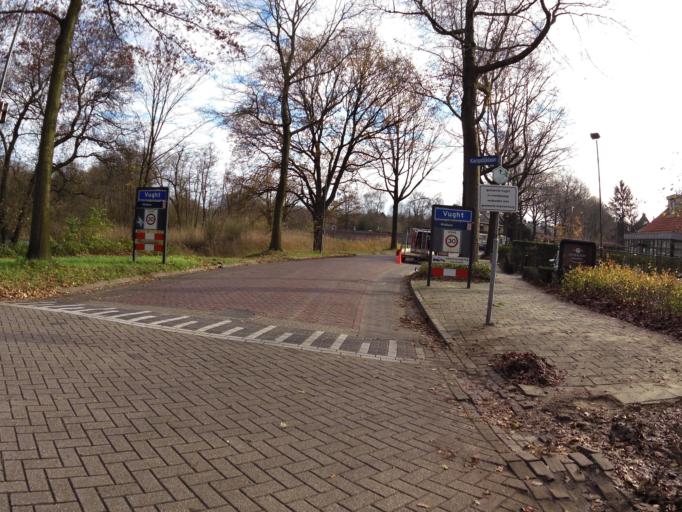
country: NL
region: North Brabant
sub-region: Gemeente Vught
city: Vught
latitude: 51.6714
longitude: 5.2849
